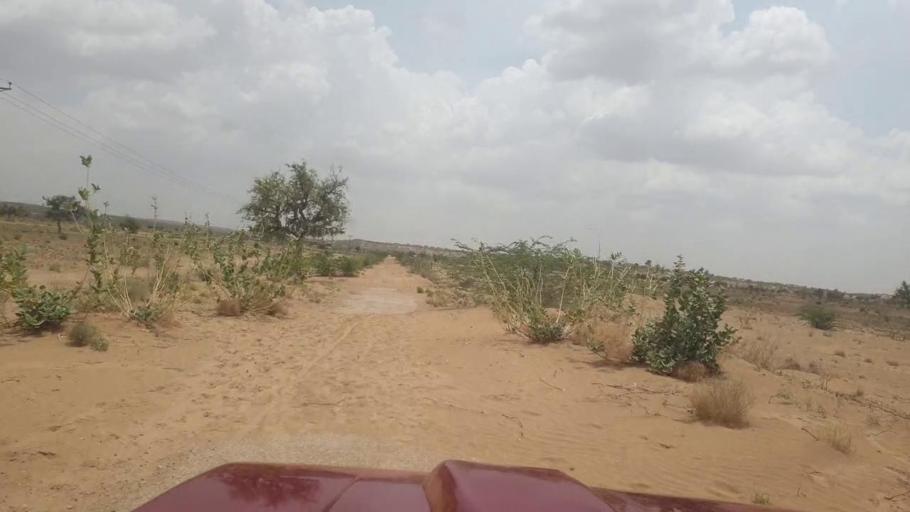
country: PK
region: Sindh
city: Islamkot
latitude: 25.1110
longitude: 70.3717
